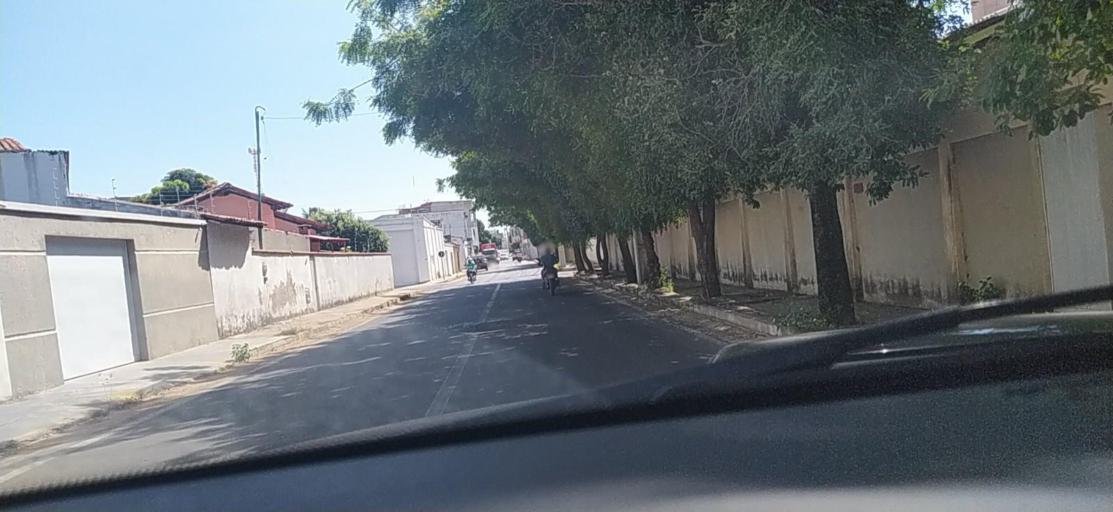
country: BR
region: Bahia
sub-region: Guanambi
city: Guanambi
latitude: -14.2163
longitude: -42.7699
